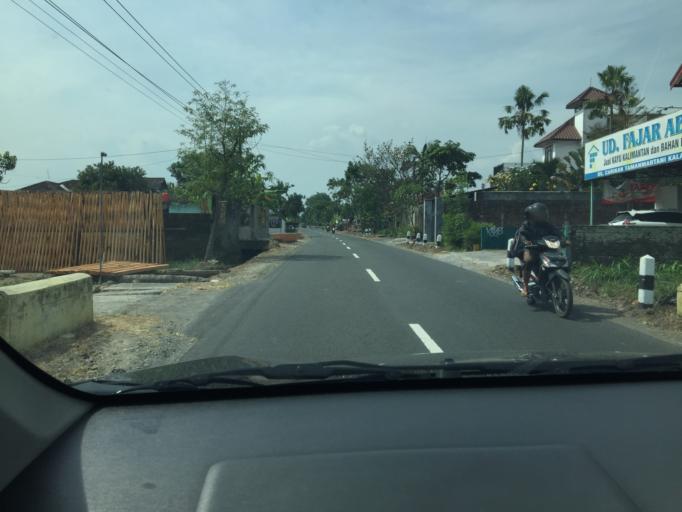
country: ID
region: Central Java
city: Candi Prambanan
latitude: -7.7497
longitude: 110.4811
